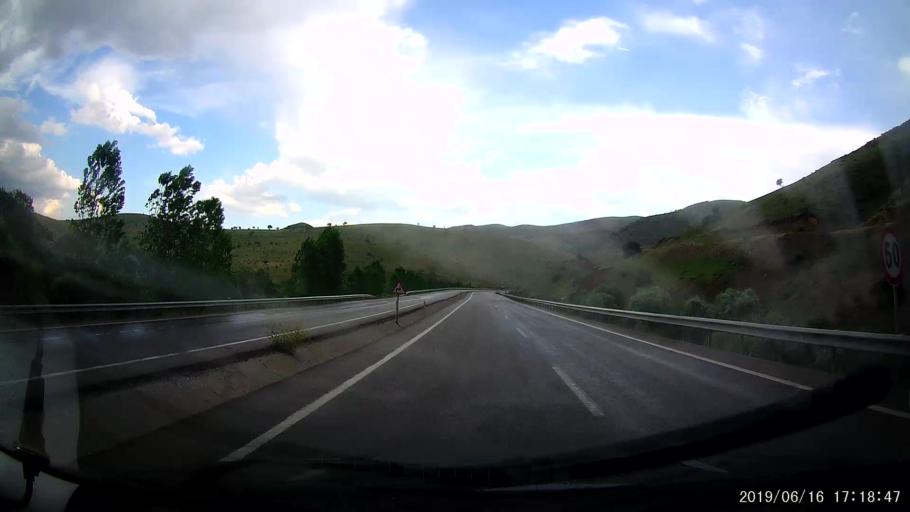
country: TR
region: Erzincan
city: Tercan
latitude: 39.8089
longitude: 40.5299
